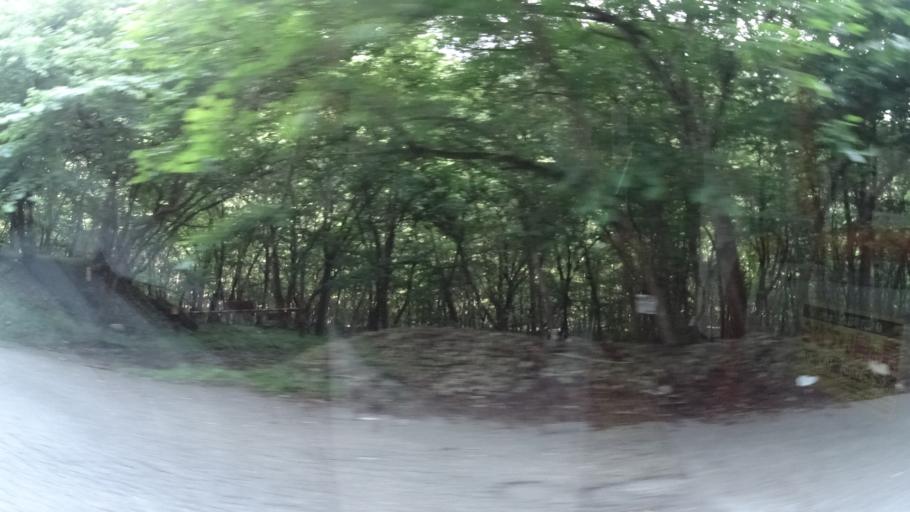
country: JP
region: Tochigi
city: Nikko
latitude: 36.6935
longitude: 139.5019
